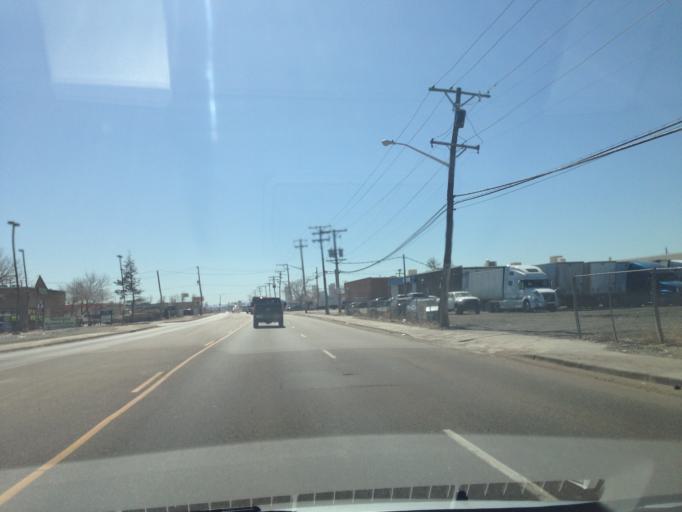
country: US
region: Colorado
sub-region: Adams County
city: Twin Lakes
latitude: 39.8000
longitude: -104.9782
